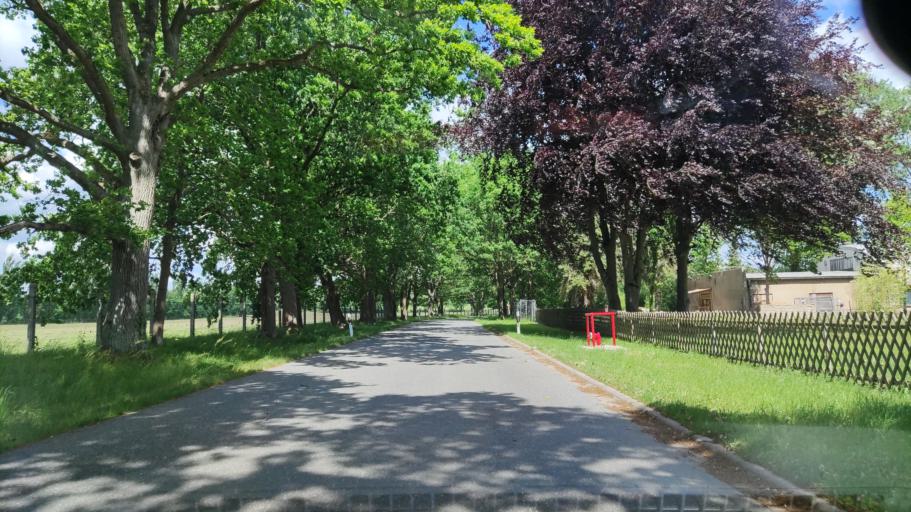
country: DE
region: Mecklenburg-Vorpommern
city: Lubtheen
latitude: 53.3878
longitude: 11.0546
